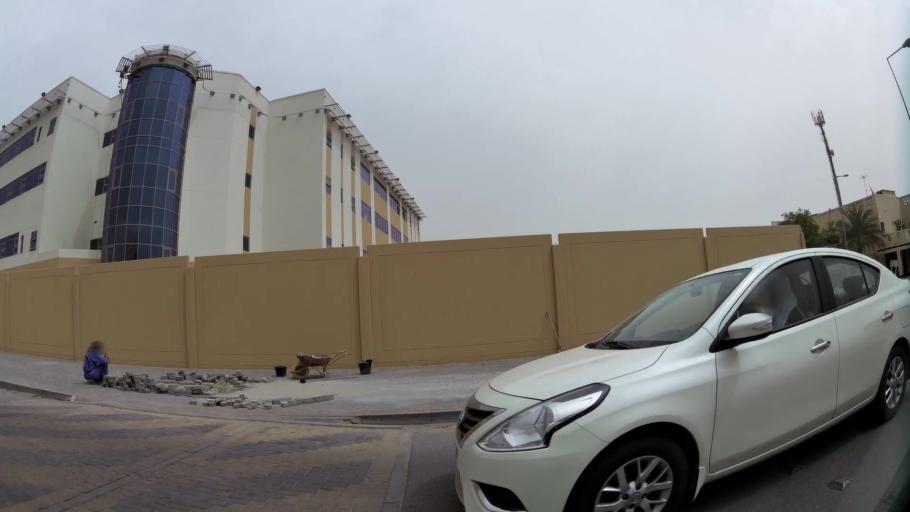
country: BH
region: Northern
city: Madinat `Isa
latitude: 26.1807
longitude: 50.5391
